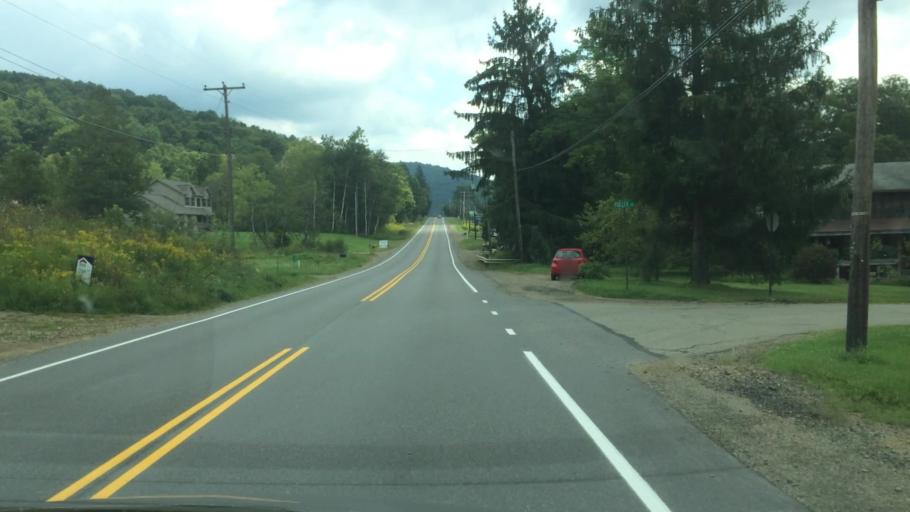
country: US
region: Pennsylvania
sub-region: McKean County
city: Bradford
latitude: 41.9095
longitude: -78.6302
